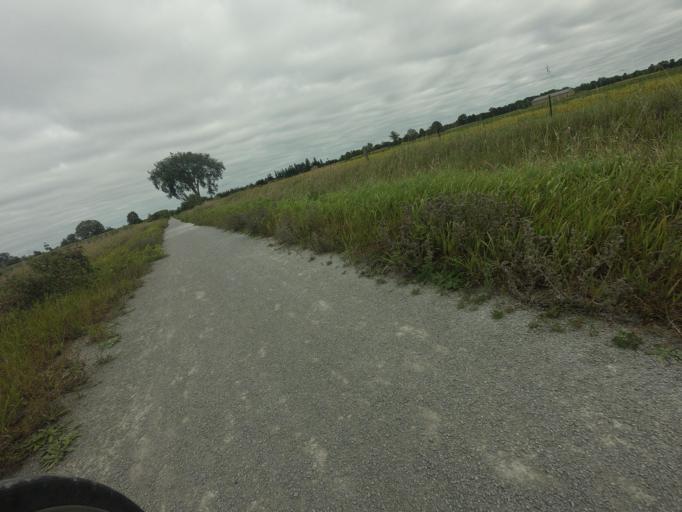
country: CA
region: Ontario
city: Omemee
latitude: 44.3144
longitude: -78.8632
